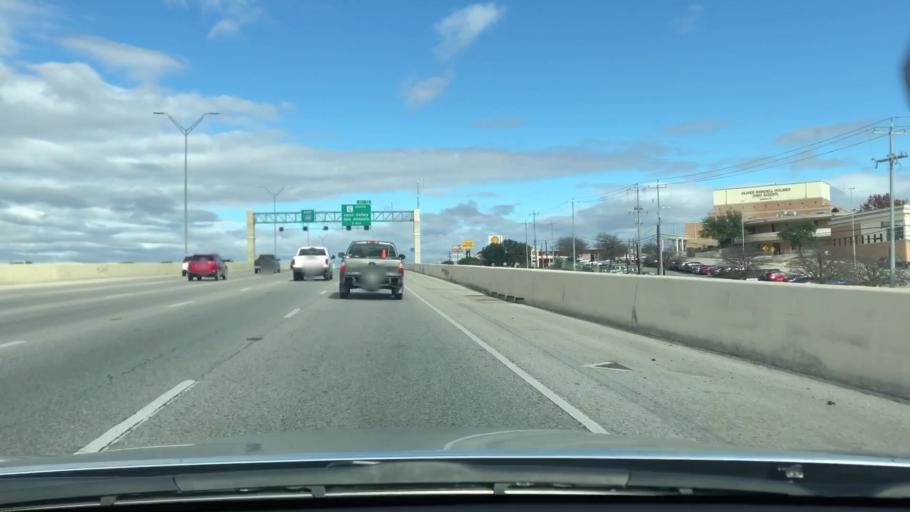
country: US
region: Texas
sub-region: Bexar County
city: Leon Valley
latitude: 29.4646
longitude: -98.6202
